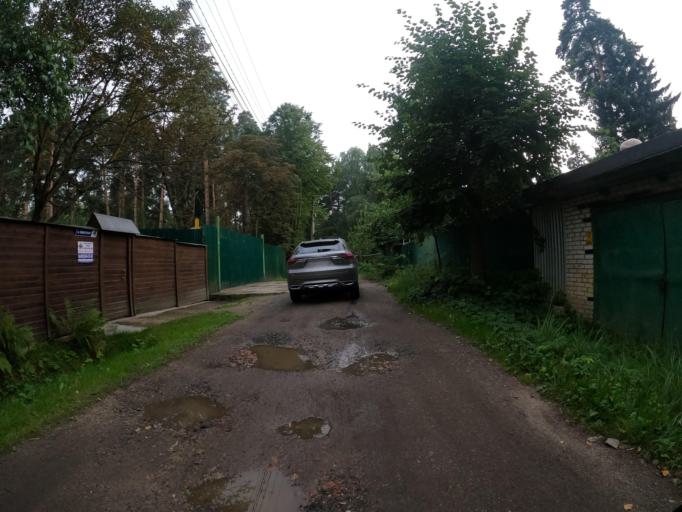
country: RU
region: Moskovskaya
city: Bykovo
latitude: 55.6457
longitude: 38.1067
